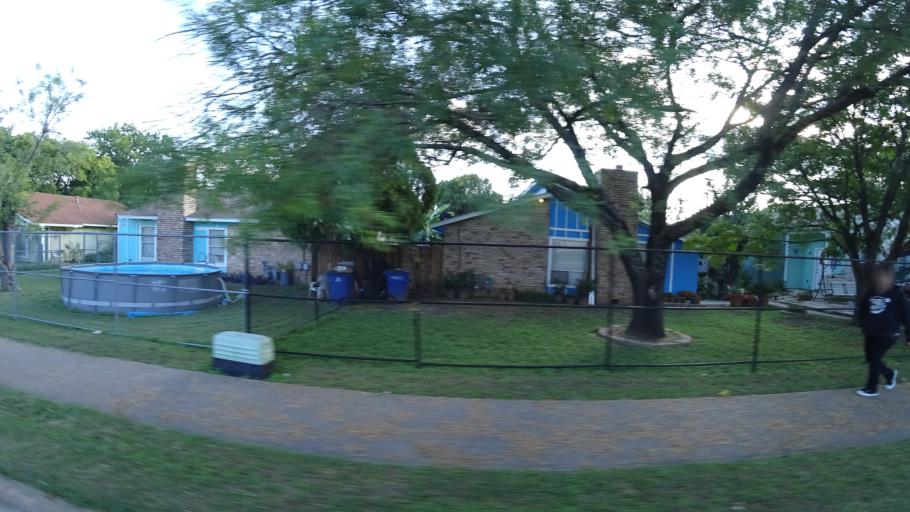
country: US
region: Texas
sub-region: Travis County
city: Wells Branch
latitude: 30.3650
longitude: -97.7012
